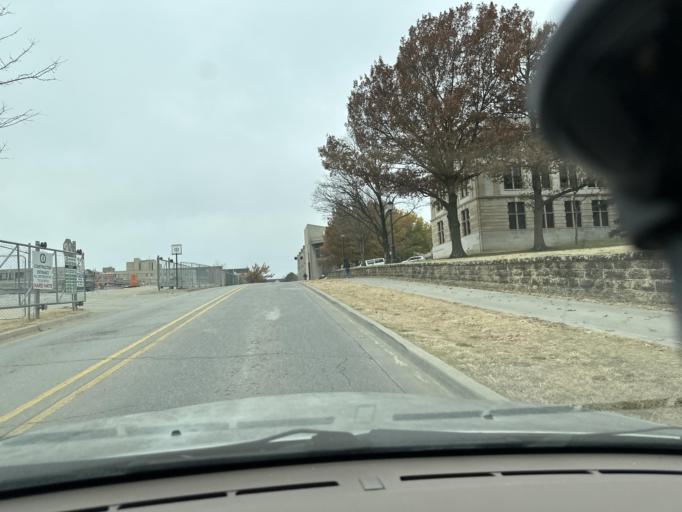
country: US
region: Arkansas
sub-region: Washington County
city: Fayetteville
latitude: 36.0666
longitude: -94.1697
